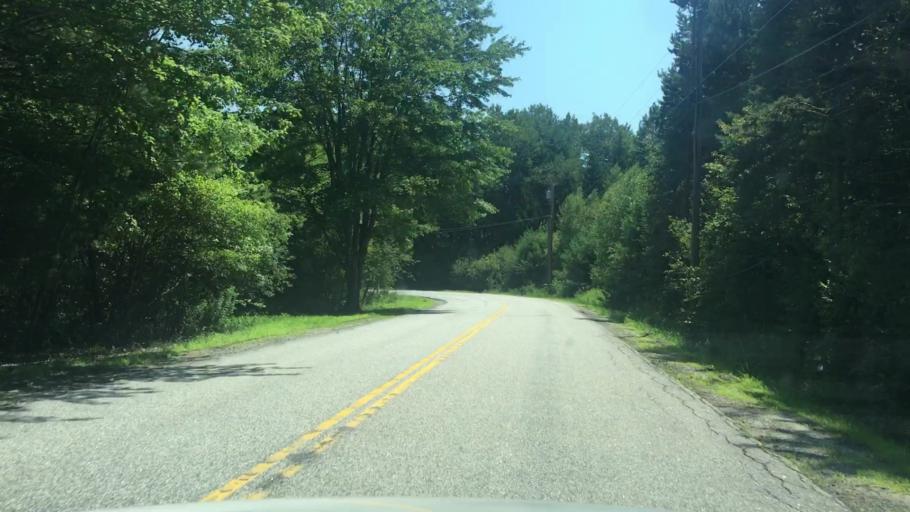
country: US
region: Maine
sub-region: Cumberland County
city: Falmouth
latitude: 43.7474
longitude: -70.2722
